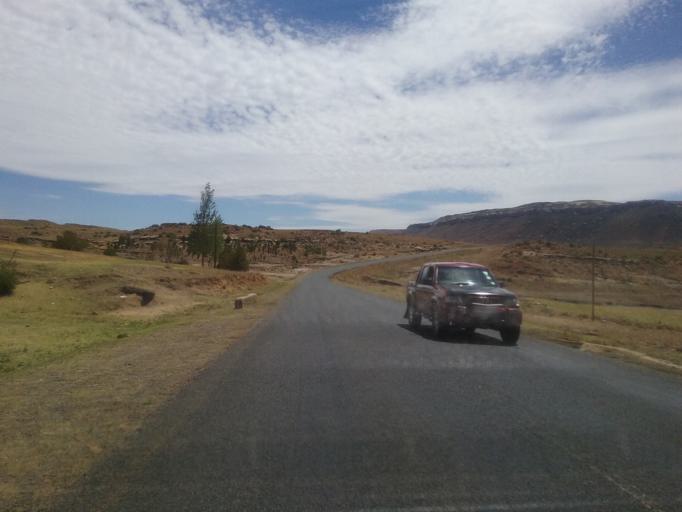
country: LS
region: Mafeteng
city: Mafeteng
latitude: -29.9036
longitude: 27.2515
